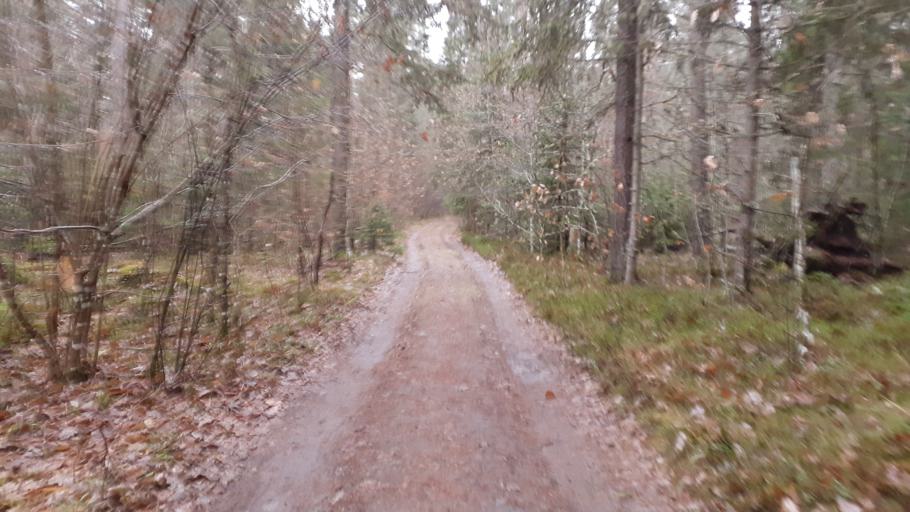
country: LV
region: Kuldigas Rajons
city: Kuldiga
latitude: 56.9991
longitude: 21.9661
